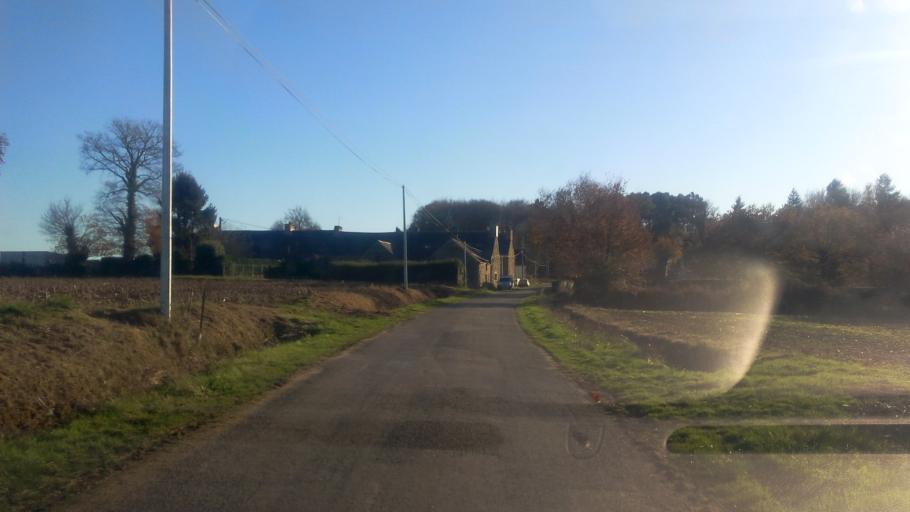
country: FR
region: Brittany
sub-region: Departement du Morbihan
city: Peillac
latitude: 47.7222
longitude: -2.2284
